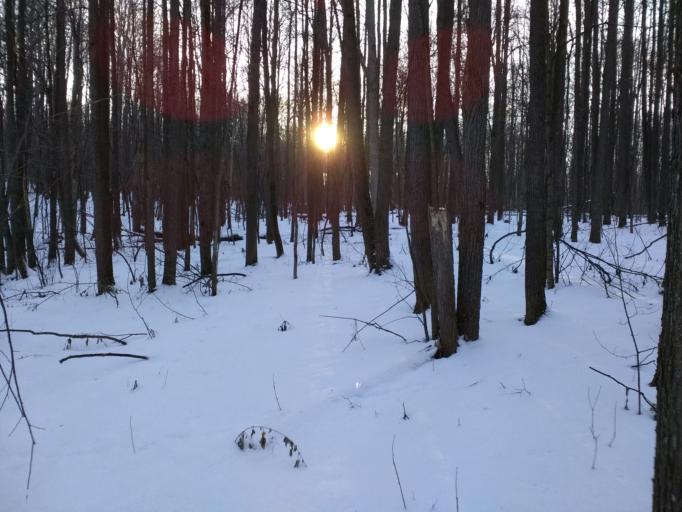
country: RU
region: Bashkortostan
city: Iglino
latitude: 54.8037
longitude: 56.5863
